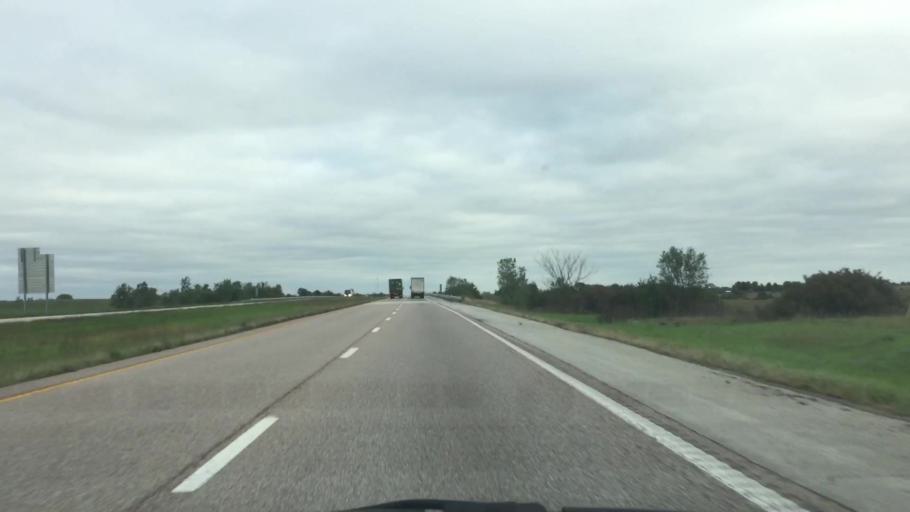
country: US
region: Missouri
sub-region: Clinton County
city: Lathrop
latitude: 39.5723
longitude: -94.2615
